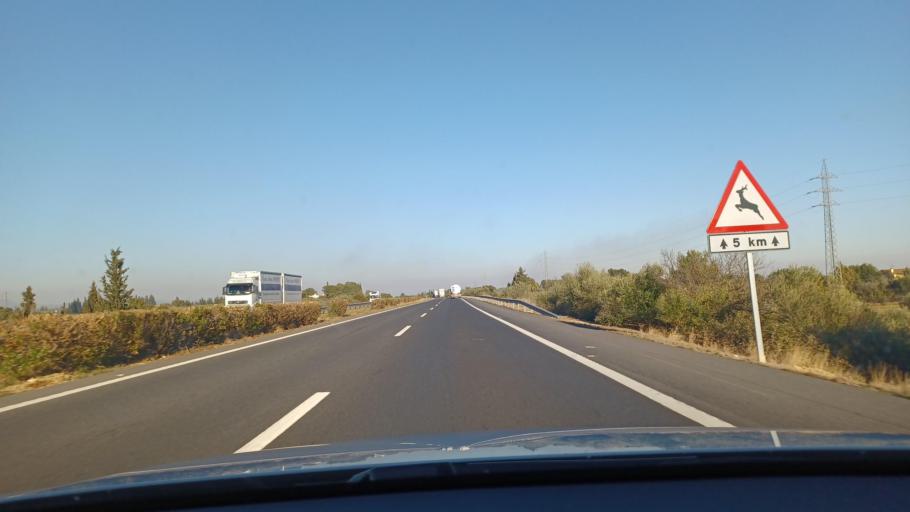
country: ES
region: Catalonia
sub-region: Provincia de Tarragona
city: Masdenverge
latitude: 40.6944
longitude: 0.5359
